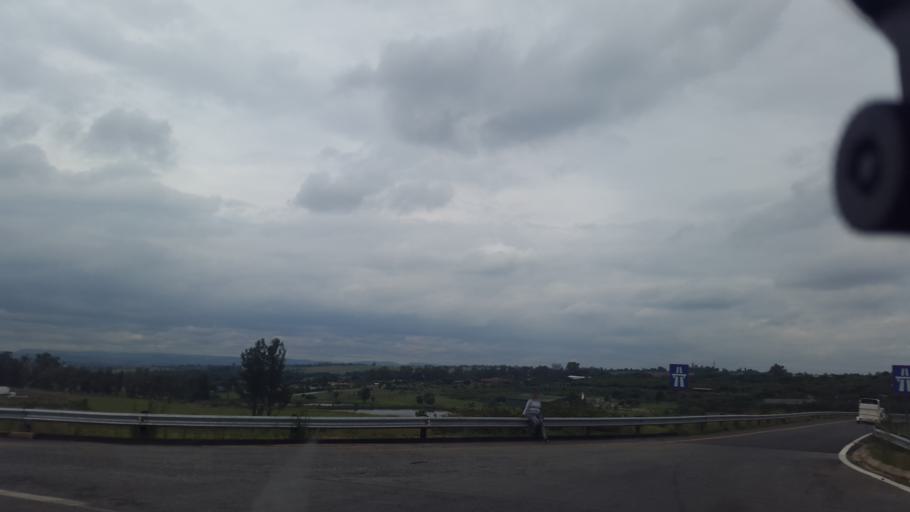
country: ZA
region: Gauteng
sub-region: West Rand District Municipality
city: Muldersdriseloop
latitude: -26.0184
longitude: 27.8598
